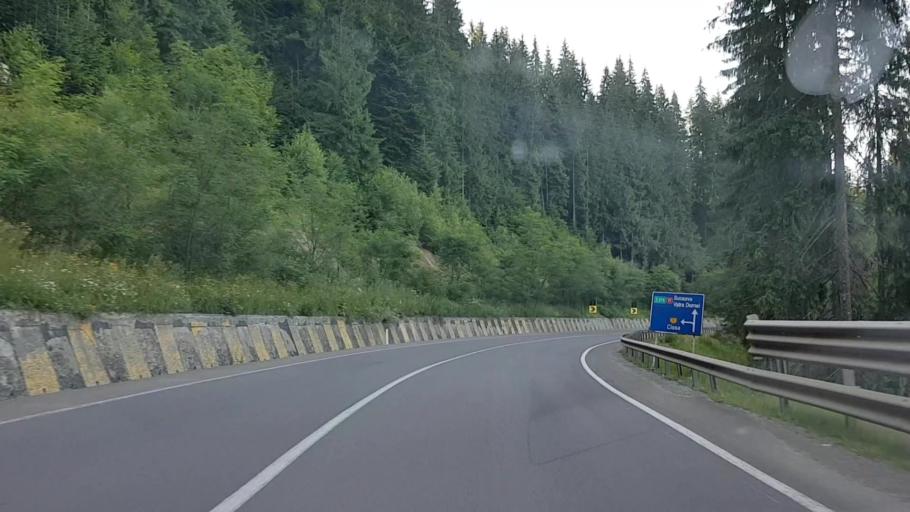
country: RO
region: Bistrita-Nasaud
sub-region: Comuna Lunca Ilvei
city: Lunca Ilvei
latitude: 47.2301
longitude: 24.9632
